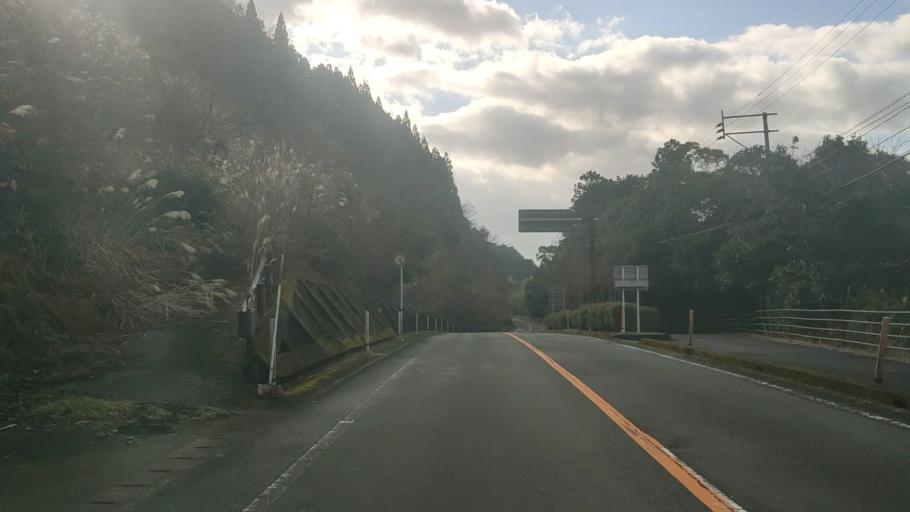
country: JP
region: Kumamoto
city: Hitoyoshi
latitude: 32.3116
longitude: 130.8478
